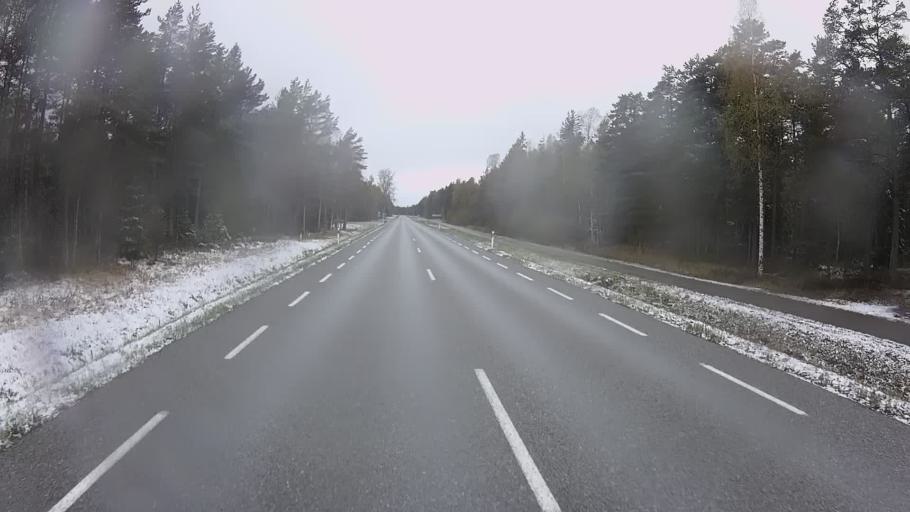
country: EE
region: Hiiumaa
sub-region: Kaerdla linn
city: Kardla
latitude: 59.0104
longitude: 22.6507
